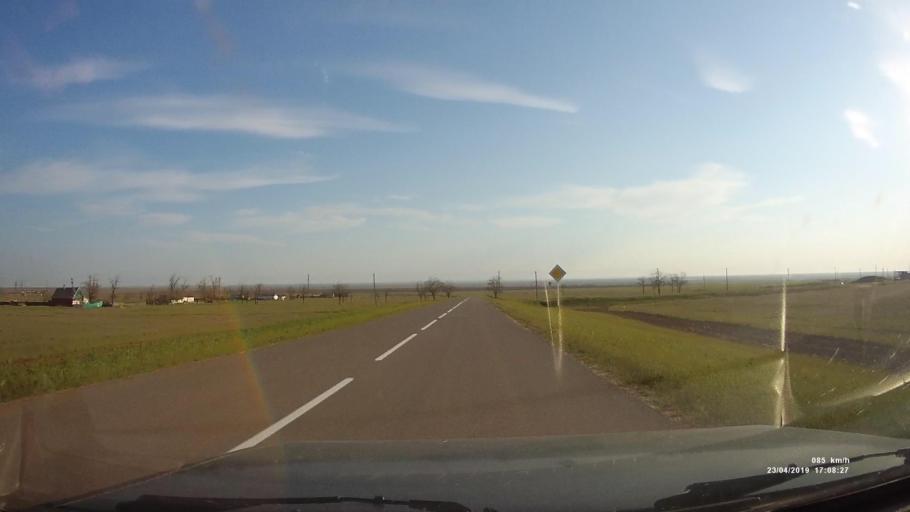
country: RU
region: Kalmykiya
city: Priyutnoye
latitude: 46.2716
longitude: 43.4878
